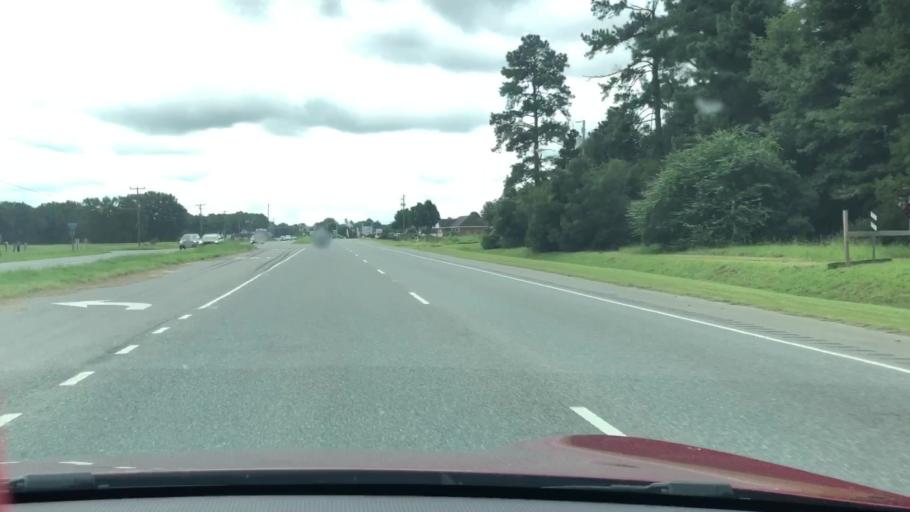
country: US
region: North Carolina
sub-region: Currituck County
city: Moyock
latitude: 36.5533
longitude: -76.1953
